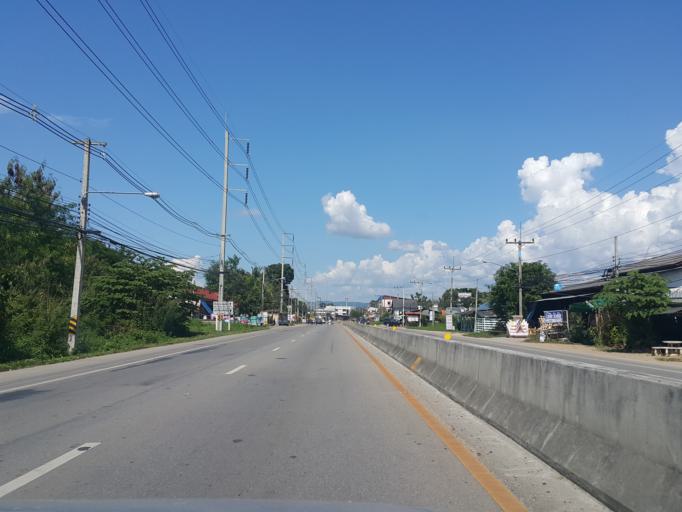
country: TH
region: Chiang Mai
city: Mae Taeng
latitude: 19.1150
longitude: 98.9402
